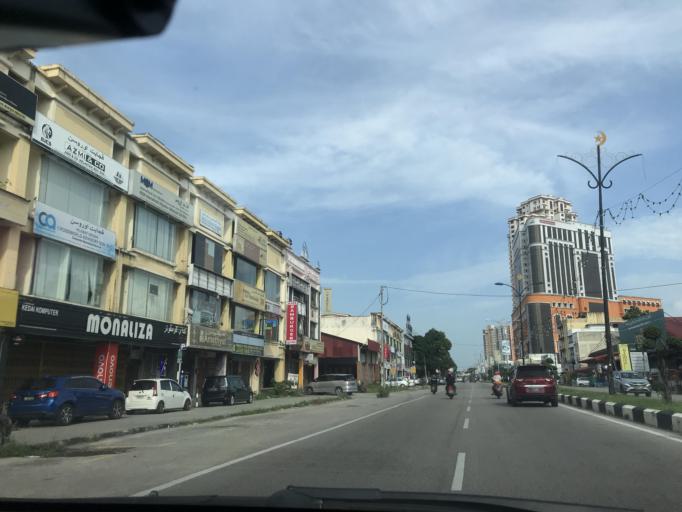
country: MY
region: Kelantan
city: Kota Bharu
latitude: 6.1158
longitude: 102.2475
